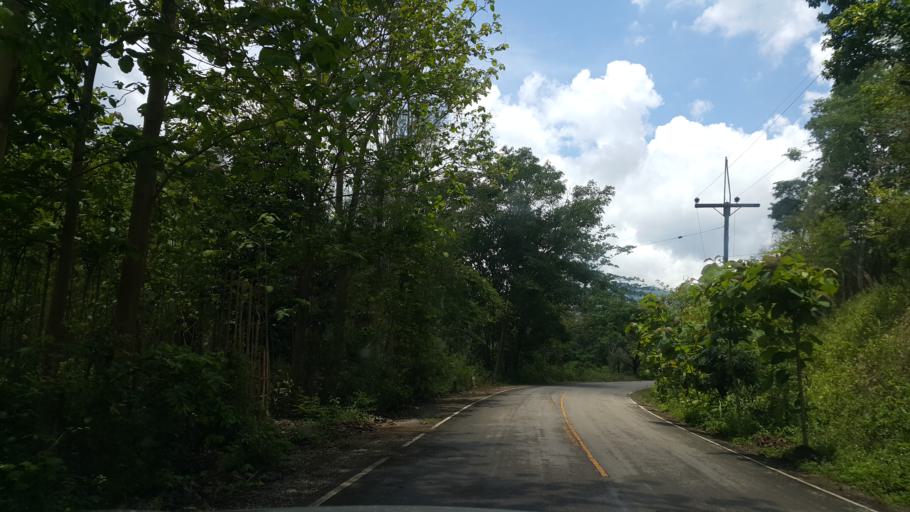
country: TH
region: Phayao
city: Phayao
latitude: 19.1886
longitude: 99.8001
